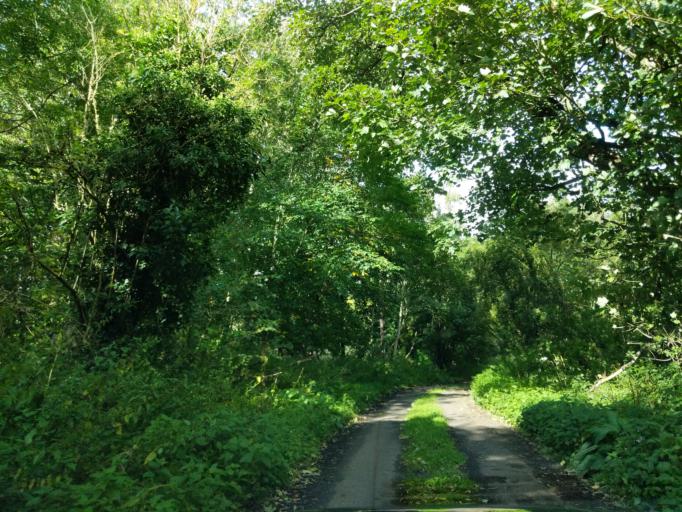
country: GB
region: Scotland
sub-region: The Scottish Borders
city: Kelso
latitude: 55.5669
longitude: -2.4729
